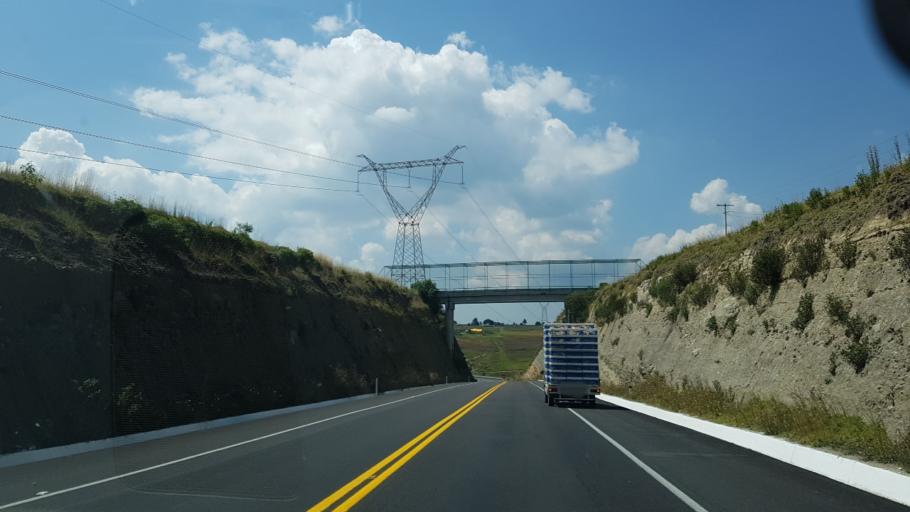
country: MX
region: Mexico
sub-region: Villa Victoria
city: Colonia Doctor Gustavo Baz
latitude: 19.3711
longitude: -99.9338
